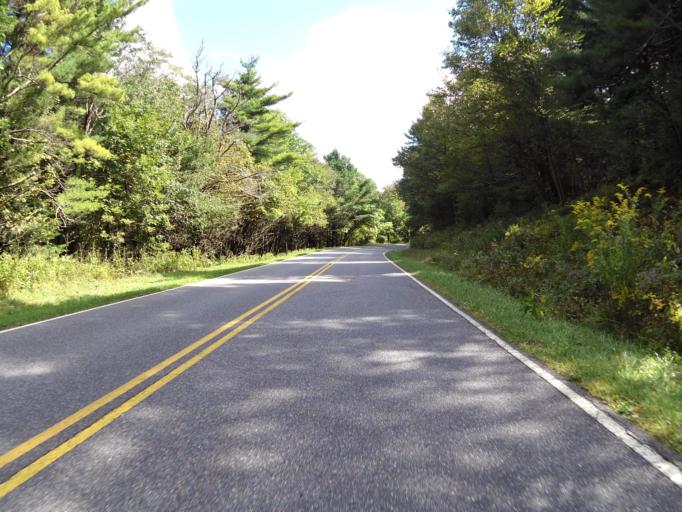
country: US
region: Virginia
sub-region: Page County
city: Luray
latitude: 38.6201
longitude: -78.3436
